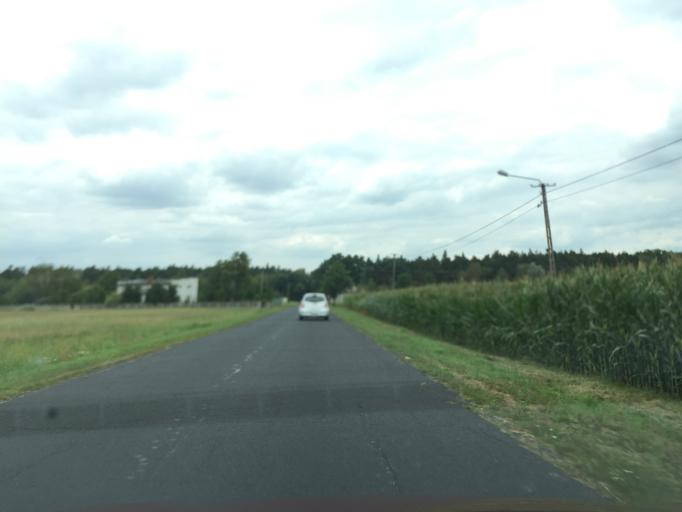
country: PL
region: Greater Poland Voivodeship
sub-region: Powiat kaliski
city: Stawiszyn
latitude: 51.9623
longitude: 18.1778
